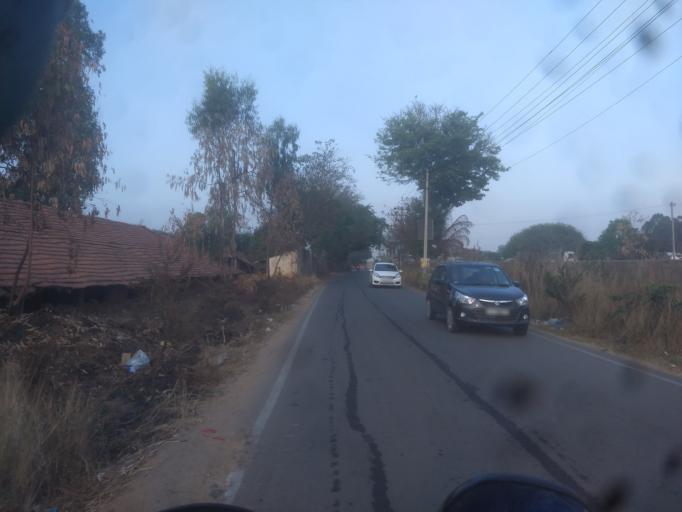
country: IN
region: Karnataka
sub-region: Bangalore Urban
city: Anekal
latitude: 12.8388
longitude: 77.7018
